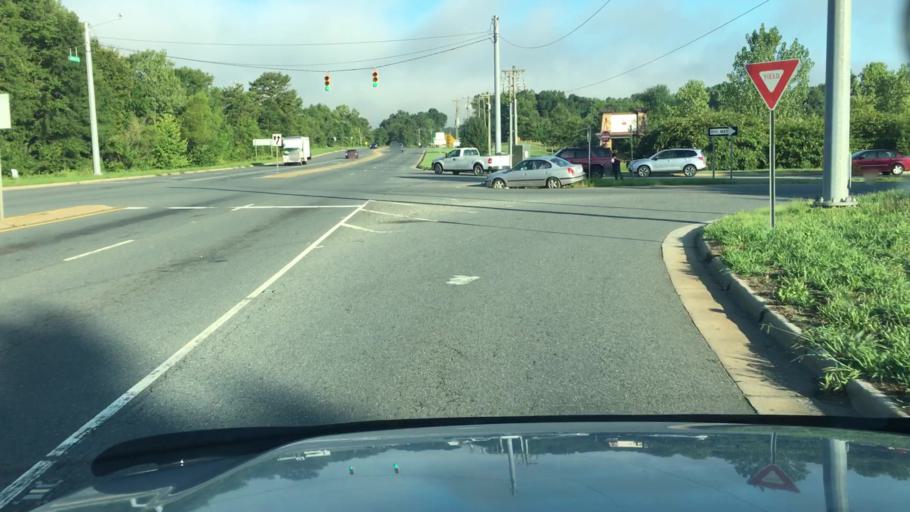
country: US
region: North Carolina
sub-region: Gaston County
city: Mount Holly
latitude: 35.2897
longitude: -80.9662
